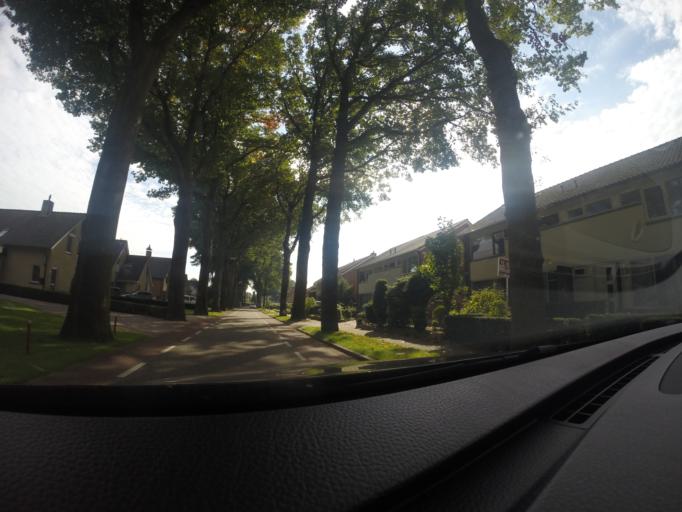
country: NL
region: Gelderland
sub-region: Gemeente Bronckhorst
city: Zelhem
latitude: 52.0103
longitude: 6.3460
